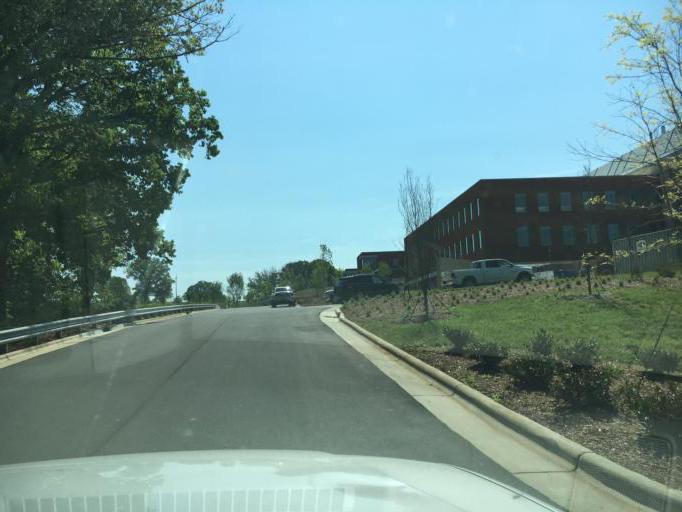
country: US
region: North Carolina
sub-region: Burke County
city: Morganton
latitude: 35.7339
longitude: -81.6800
